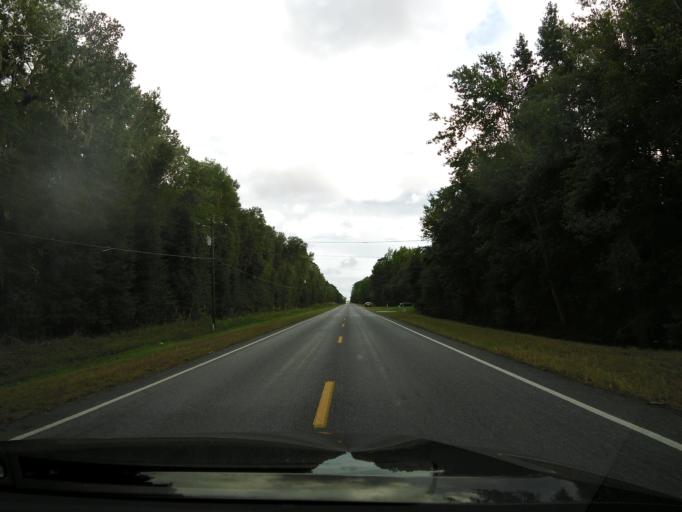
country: US
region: Georgia
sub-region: Liberty County
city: Midway
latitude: 31.6829
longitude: -81.4062
